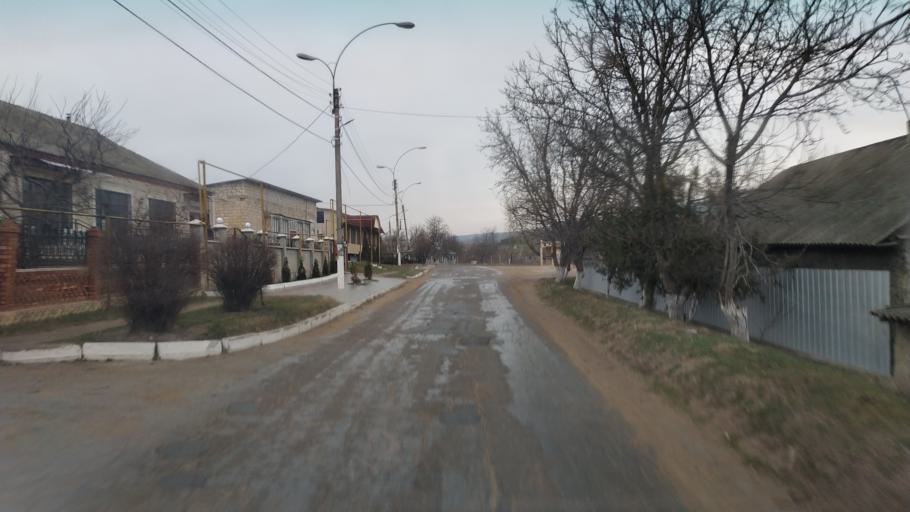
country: MD
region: Chisinau
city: Singera
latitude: 46.8298
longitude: 28.9772
